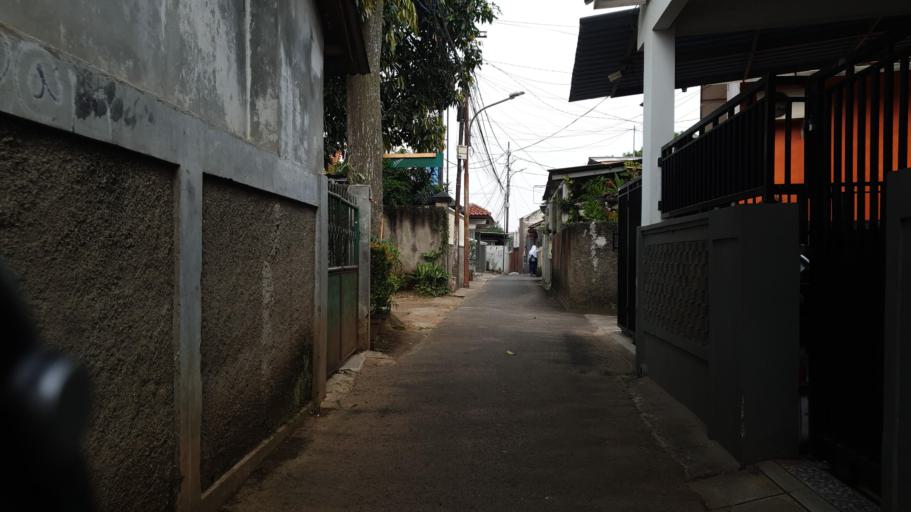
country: ID
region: West Java
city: Depok
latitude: -6.3342
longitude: 106.8236
